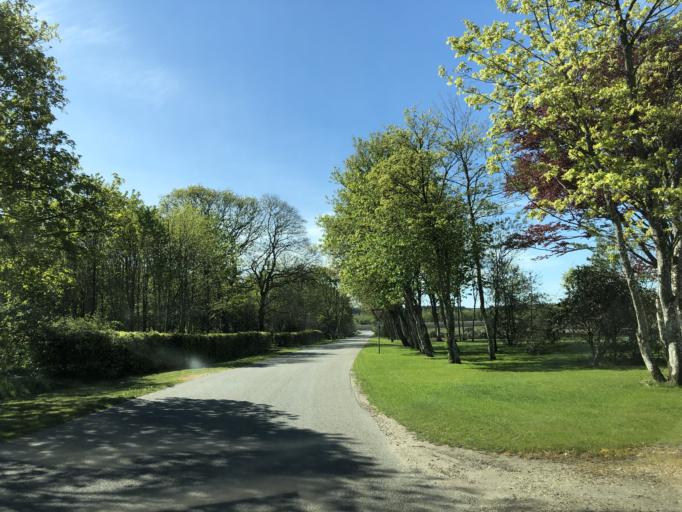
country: DK
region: Central Jutland
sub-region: Ringkobing-Skjern Kommune
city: Videbaek
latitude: 56.1816
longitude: 8.5171
